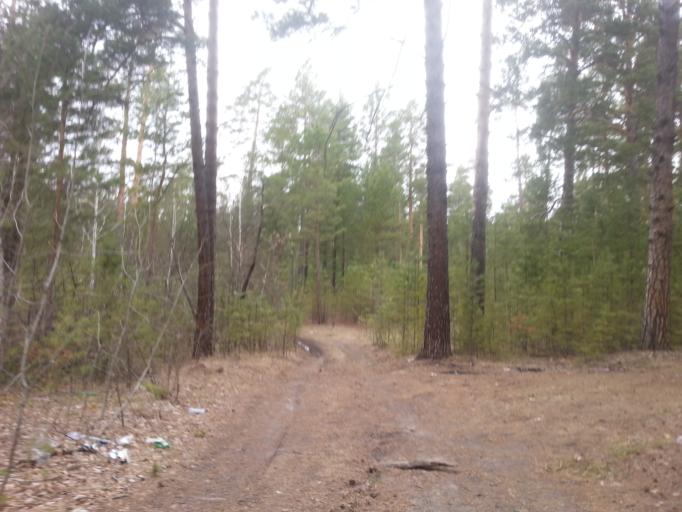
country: RU
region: Altai Krai
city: Yuzhnyy
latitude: 53.3125
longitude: 83.6967
